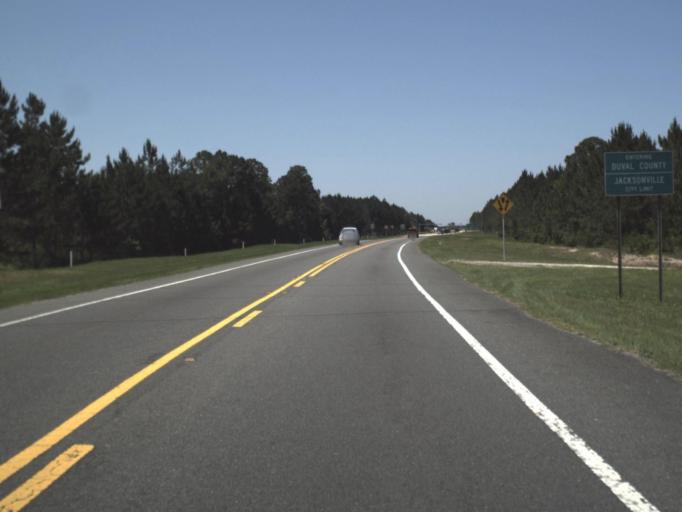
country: US
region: Florida
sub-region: Clay County
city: Lakeside
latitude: 30.1884
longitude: -81.8375
